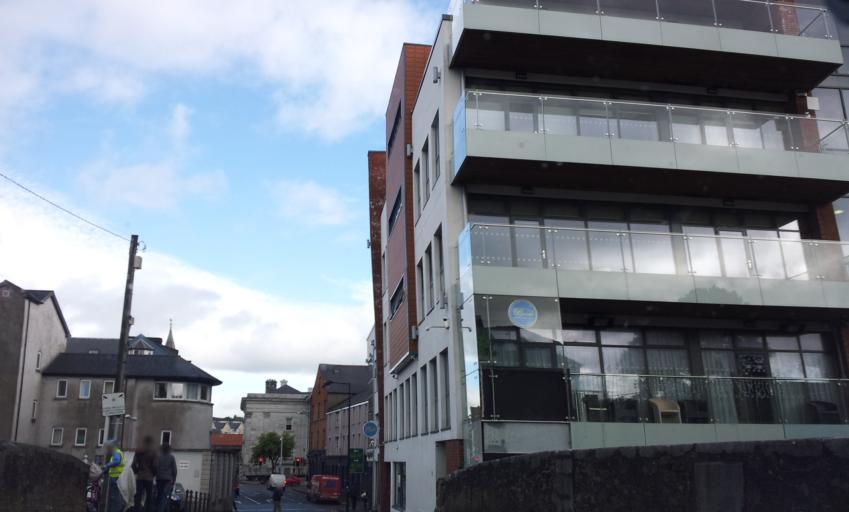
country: IE
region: Munster
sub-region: County Cork
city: Cork
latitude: 51.8965
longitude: -8.4789
